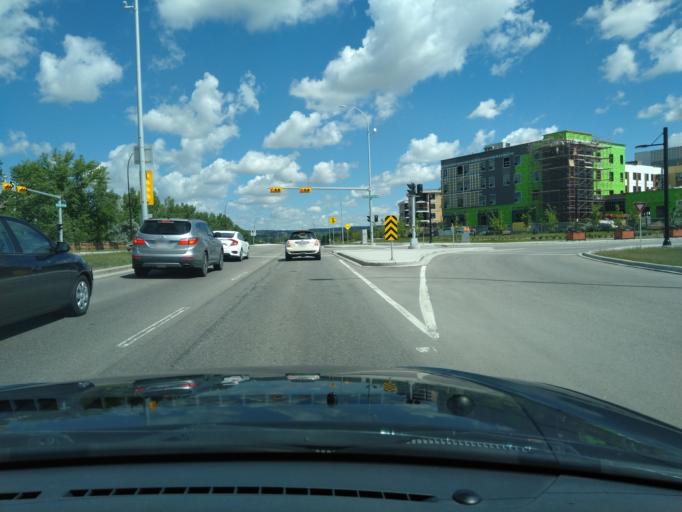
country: CA
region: Alberta
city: Calgary
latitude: 51.0764
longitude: -114.1521
